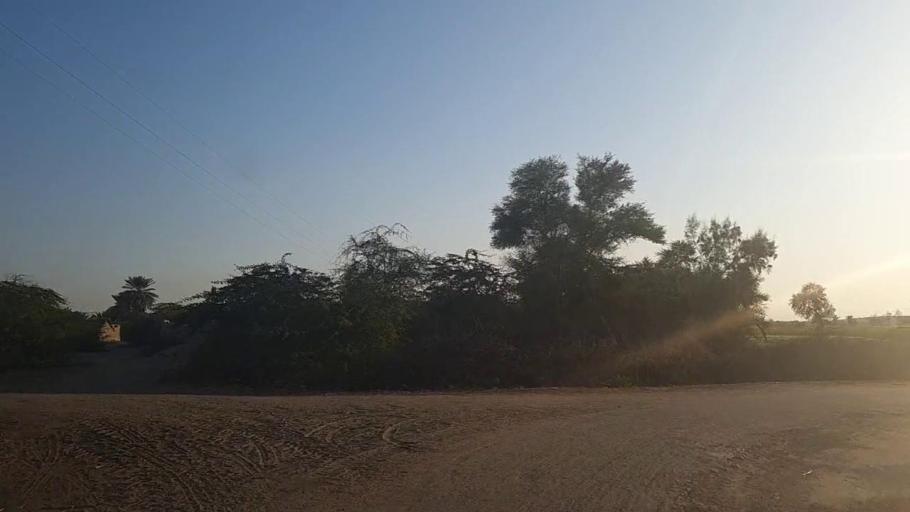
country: PK
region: Sindh
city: Jam Sahib
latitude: 26.3309
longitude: 68.6980
